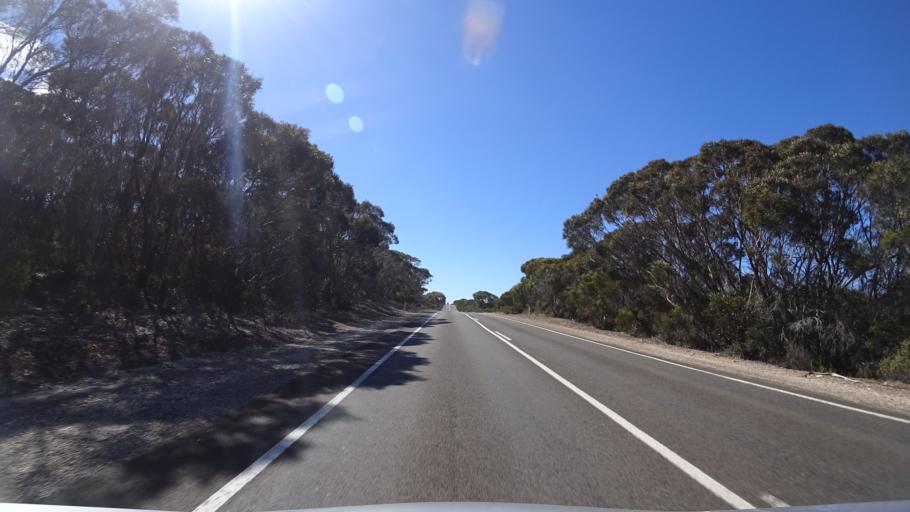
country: AU
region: South Australia
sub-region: Kangaroo Island
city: Kingscote
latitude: -35.7688
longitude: 137.6208
